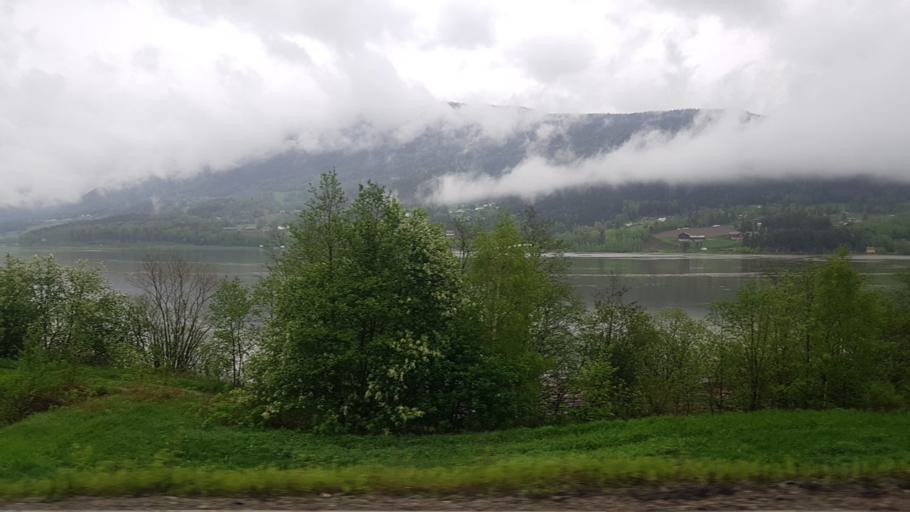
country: NO
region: Oppland
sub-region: Ringebu
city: Ringebu
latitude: 61.4268
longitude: 10.2082
